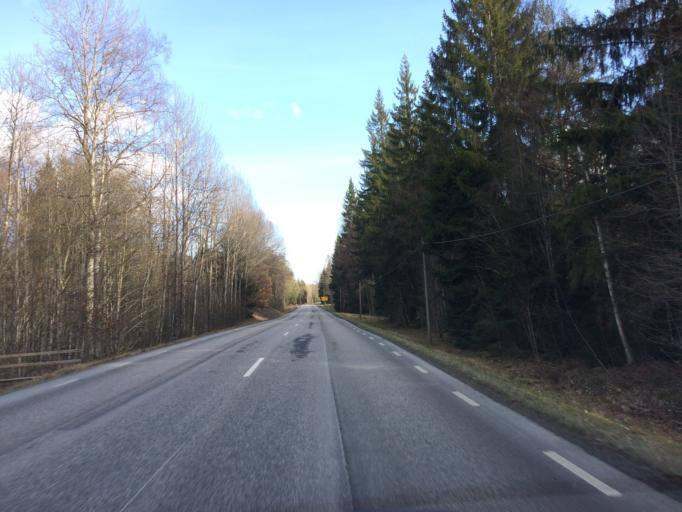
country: SE
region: Kronoberg
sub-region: Almhults Kommun
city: AElmhult
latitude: 56.5983
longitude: 14.0870
